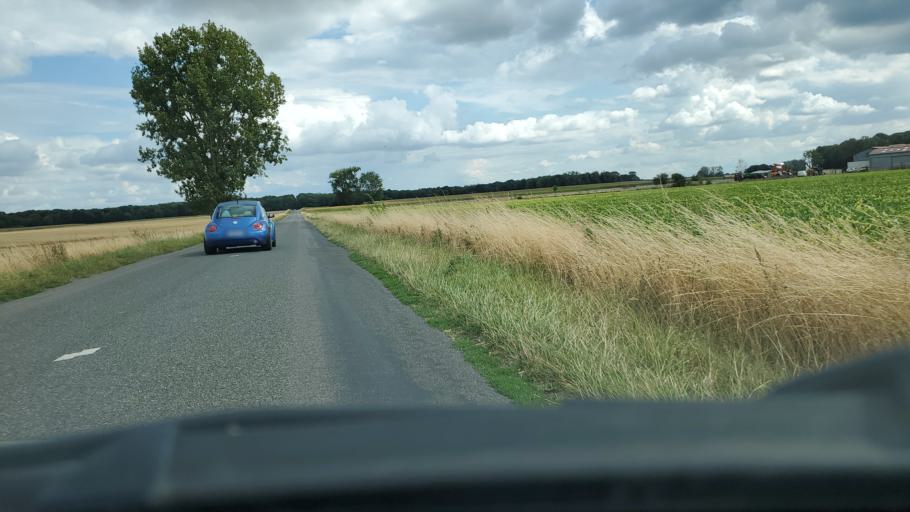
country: FR
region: Ile-de-France
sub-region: Departement de Seine-et-Marne
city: Pommeuse
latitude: 48.8673
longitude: 2.9966
